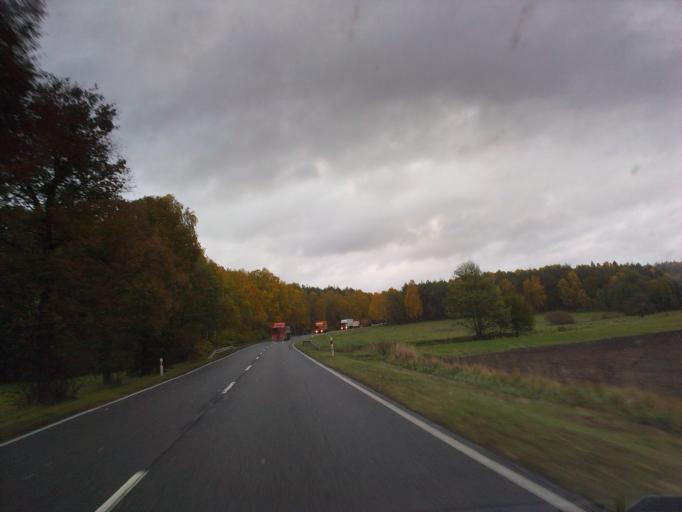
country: PL
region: Kujawsko-Pomorskie
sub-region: Powiat swiecki
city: Bukowiec
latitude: 53.4469
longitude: 18.2592
